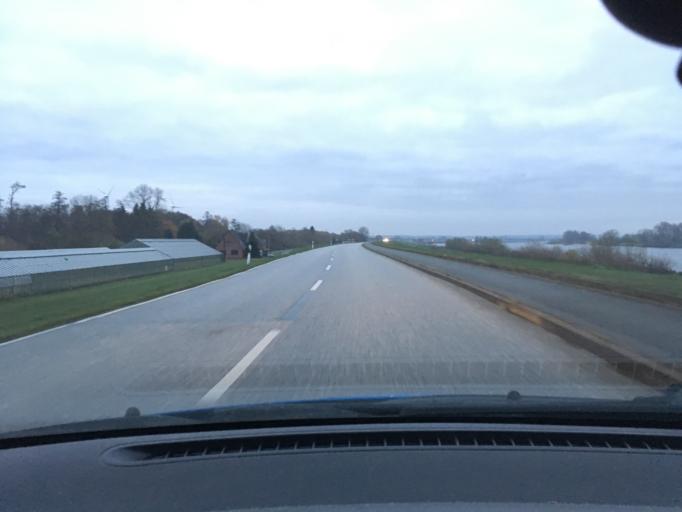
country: DE
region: Lower Saxony
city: Drage
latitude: 53.4042
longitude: 10.2436
